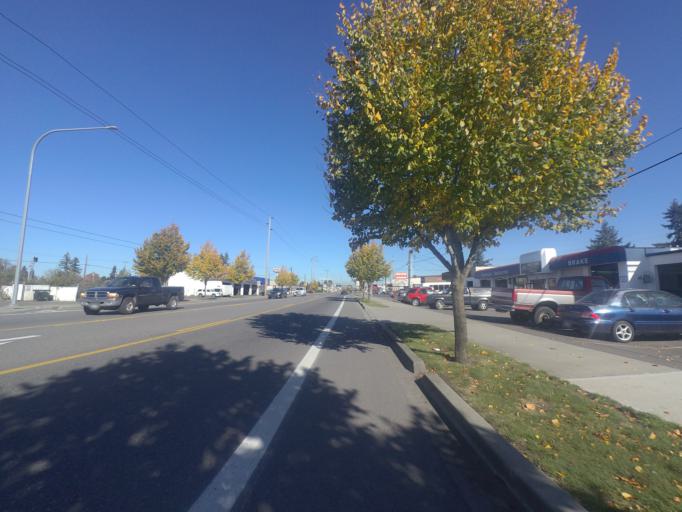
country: US
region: Washington
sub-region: Pierce County
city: McChord Air Force Base
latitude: 47.1477
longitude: -122.5071
